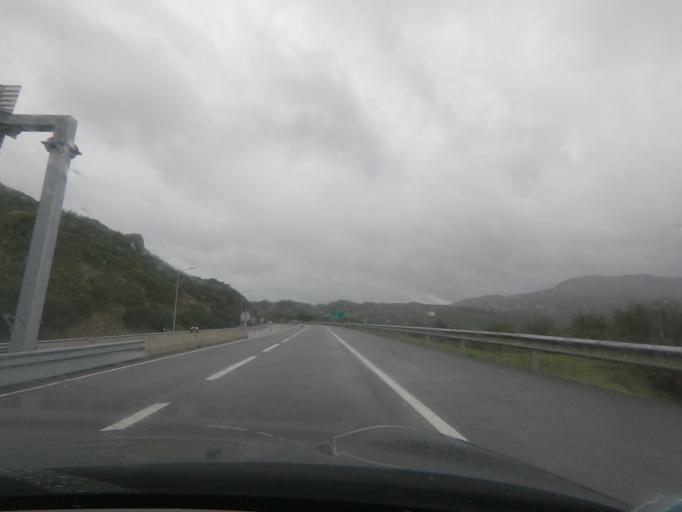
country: PT
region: Vila Real
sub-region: Vila Real
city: Vila Real
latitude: 41.2753
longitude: -7.7832
